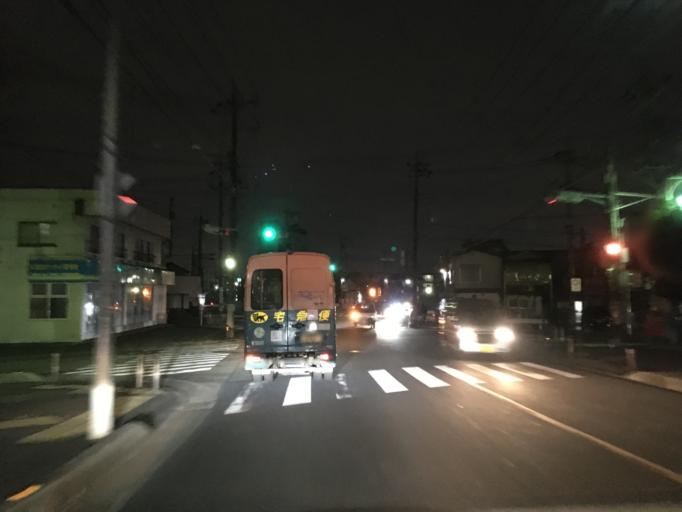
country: JP
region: Saitama
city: Sayama
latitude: 35.8674
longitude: 139.3979
